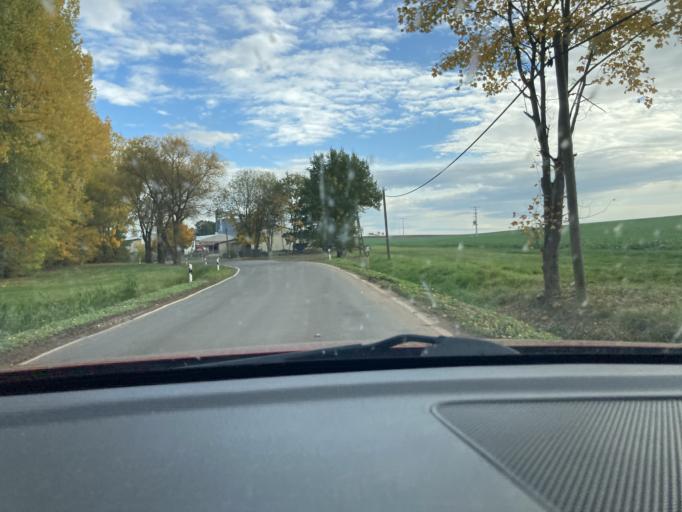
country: DE
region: Thuringia
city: Friedrichsthal
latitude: 51.5192
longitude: 10.5743
